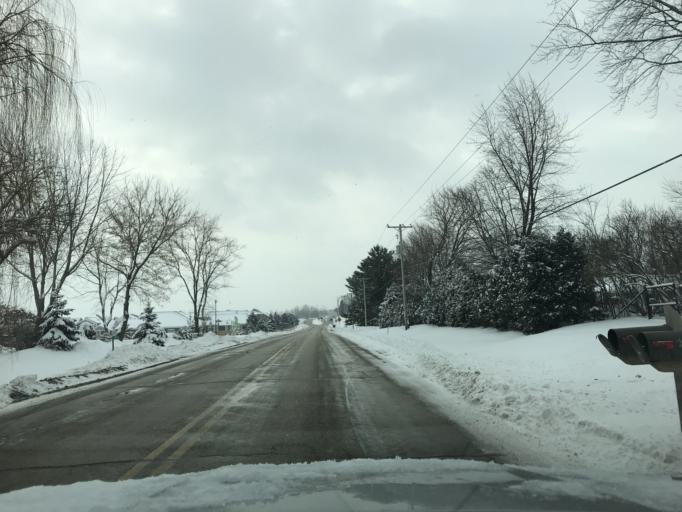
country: US
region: Wisconsin
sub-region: Dane County
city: Sun Prairie
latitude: 43.1686
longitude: -89.2854
